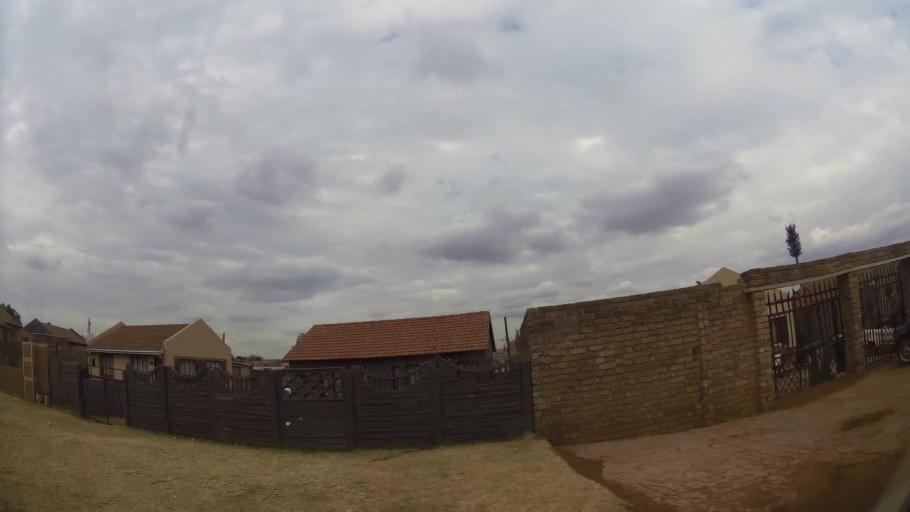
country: ZA
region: Gauteng
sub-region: Ekurhuleni Metropolitan Municipality
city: Germiston
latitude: -26.3841
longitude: 28.1269
